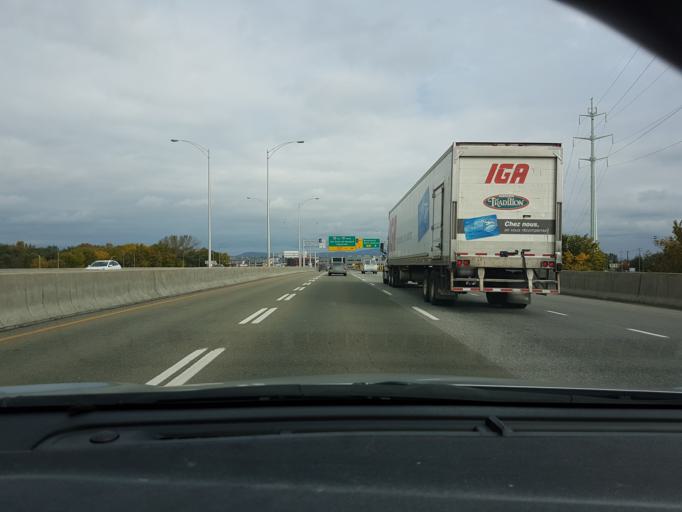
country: CA
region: Quebec
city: L'Ancienne-Lorette
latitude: 46.8103
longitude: -71.2892
